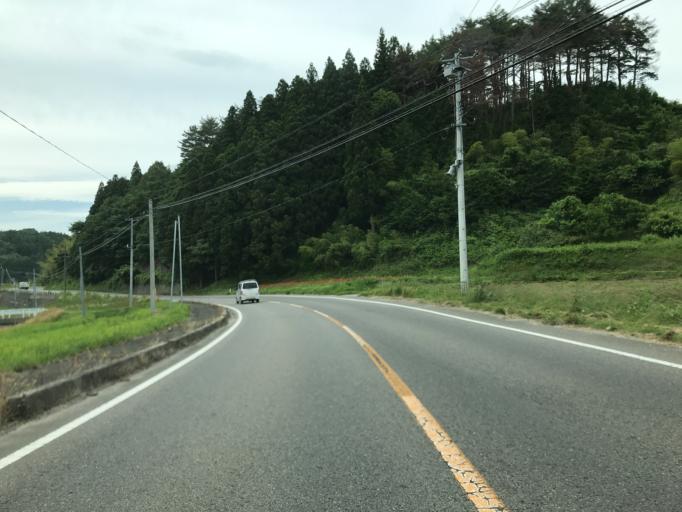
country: JP
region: Fukushima
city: Funehikimachi-funehiki
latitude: 37.4508
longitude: 140.7694
